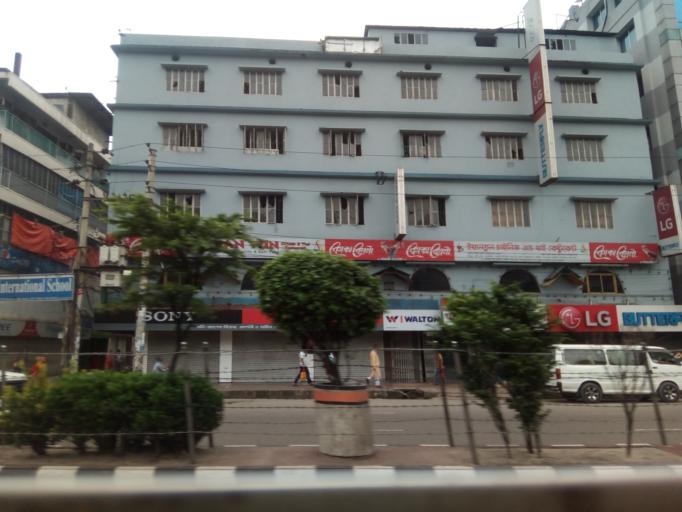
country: BD
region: Dhaka
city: Azimpur
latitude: 23.7617
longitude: 90.3893
